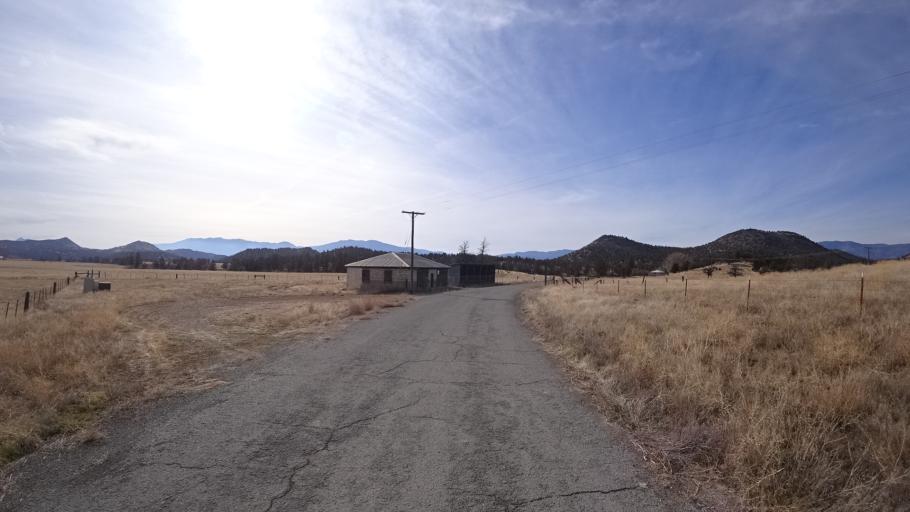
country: US
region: California
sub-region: Siskiyou County
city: Montague
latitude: 41.5927
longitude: -122.4332
